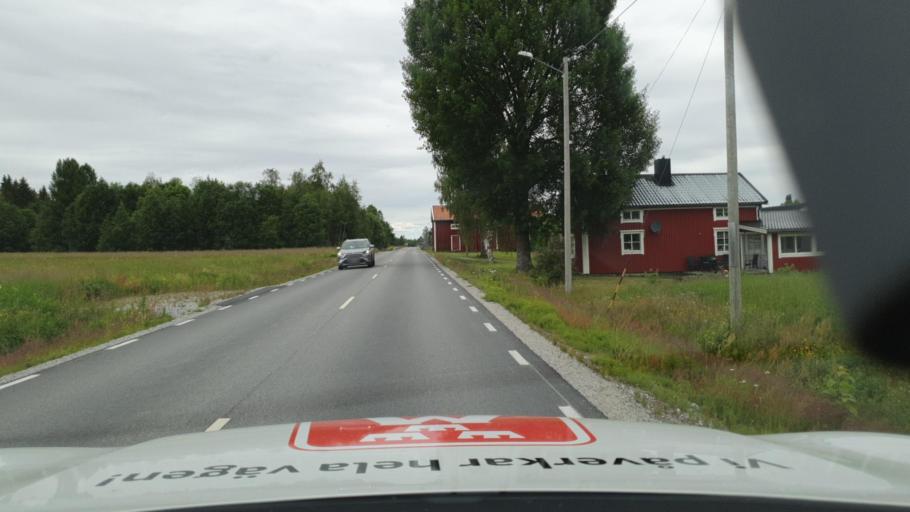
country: SE
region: Vaesterbotten
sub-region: Nordmalings Kommun
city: Nordmaling
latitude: 63.5365
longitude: 19.3665
